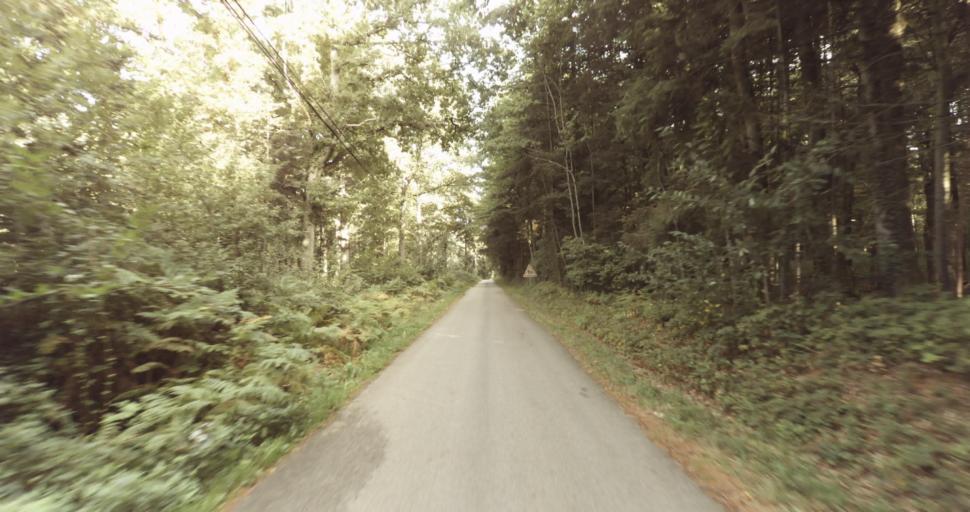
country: FR
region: Lower Normandy
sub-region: Departement de l'Orne
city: Gace
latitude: 48.8231
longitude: 0.2334
